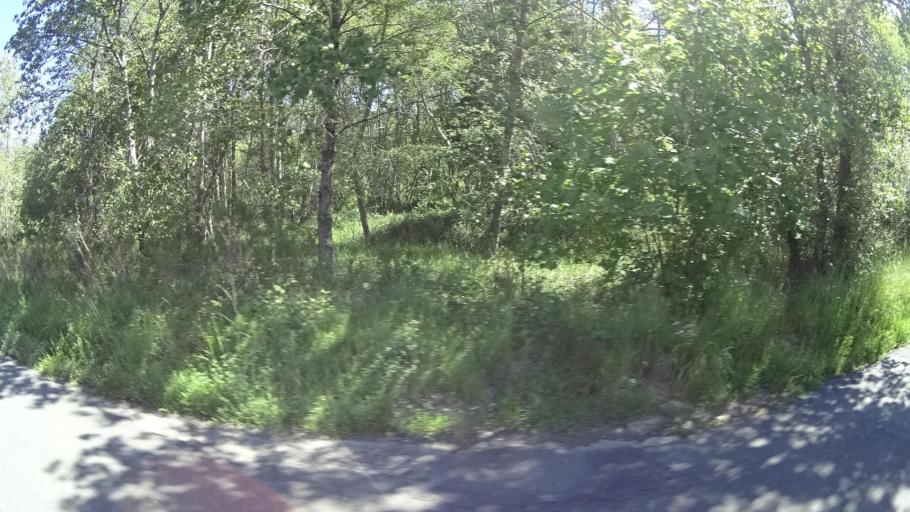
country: US
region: California
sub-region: Humboldt County
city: Rio Dell
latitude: 40.2349
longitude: -124.1174
